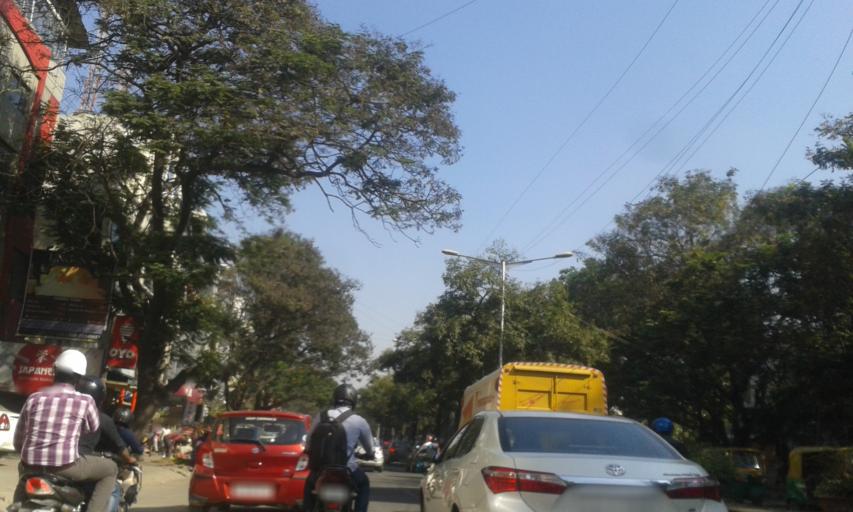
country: IN
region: Karnataka
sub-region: Bangalore Urban
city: Bangalore
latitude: 12.9563
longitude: 77.5923
